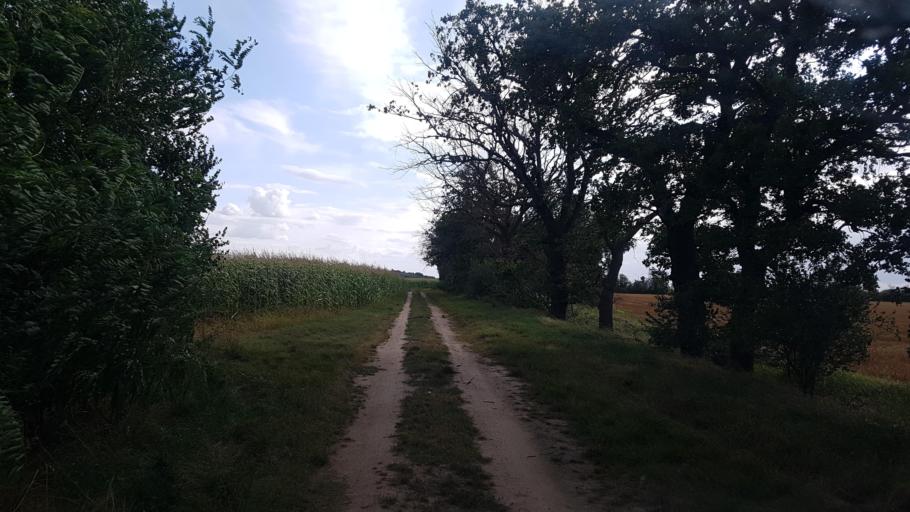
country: DE
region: Brandenburg
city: Bad Liebenwerda
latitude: 51.5106
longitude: 13.3020
